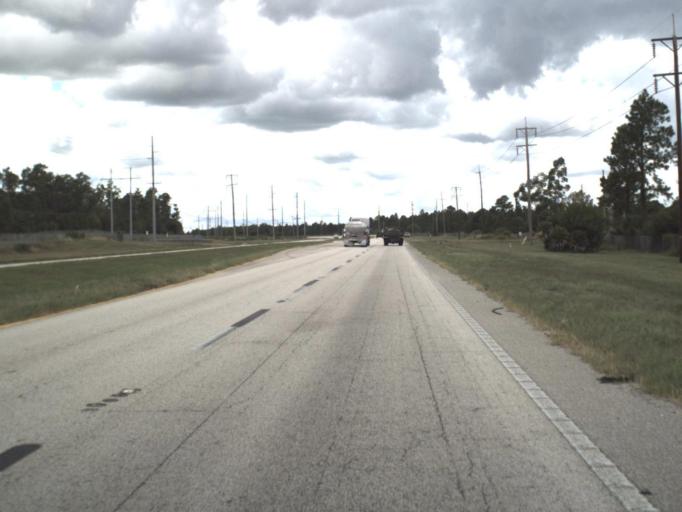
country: US
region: Florida
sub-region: Polk County
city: Bartow
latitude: 27.8985
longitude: -81.9022
